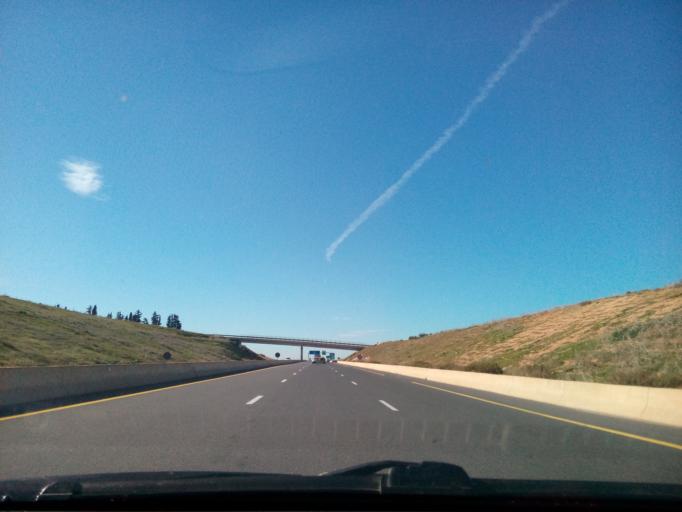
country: DZ
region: Tlemcen
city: Bensekrane
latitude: 34.9920
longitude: -1.2041
